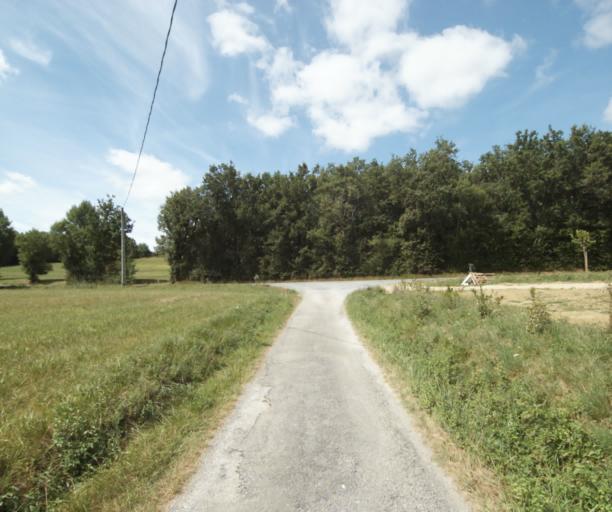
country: FR
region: Midi-Pyrenees
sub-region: Departement du Tarn
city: Soreze
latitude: 43.4763
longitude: 2.0765
